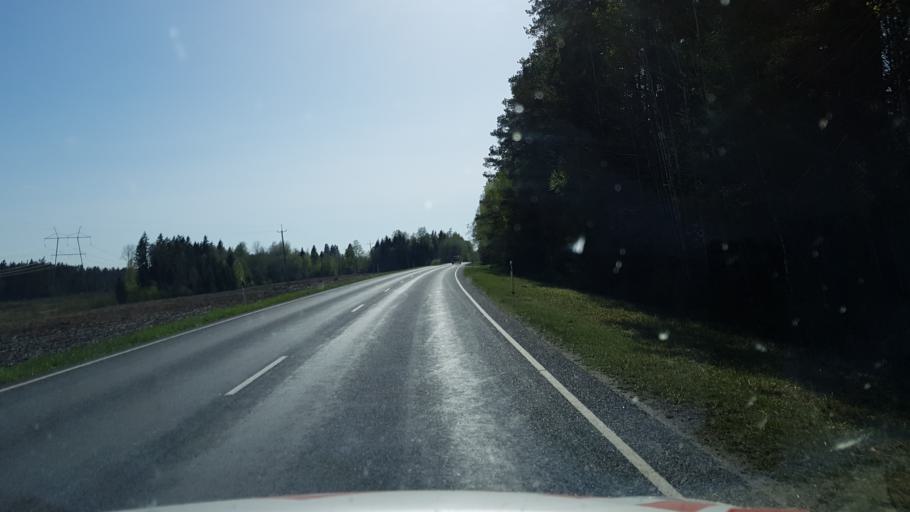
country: EE
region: Viljandimaa
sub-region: Abja vald
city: Abja-Paluoja
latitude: 58.2669
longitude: 25.2584
